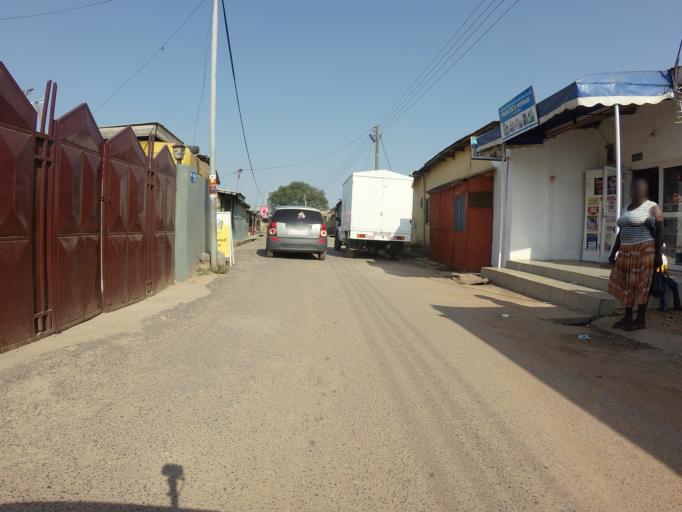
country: GH
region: Greater Accra
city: Dome
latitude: 5.6126
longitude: -0.2422
